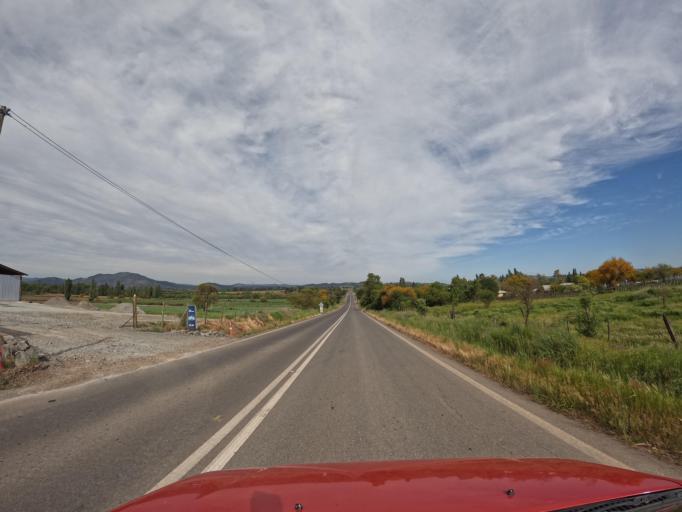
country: CL
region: Maule
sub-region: Provincia de Talca
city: Talca
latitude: -35.3752
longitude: -71.8360
